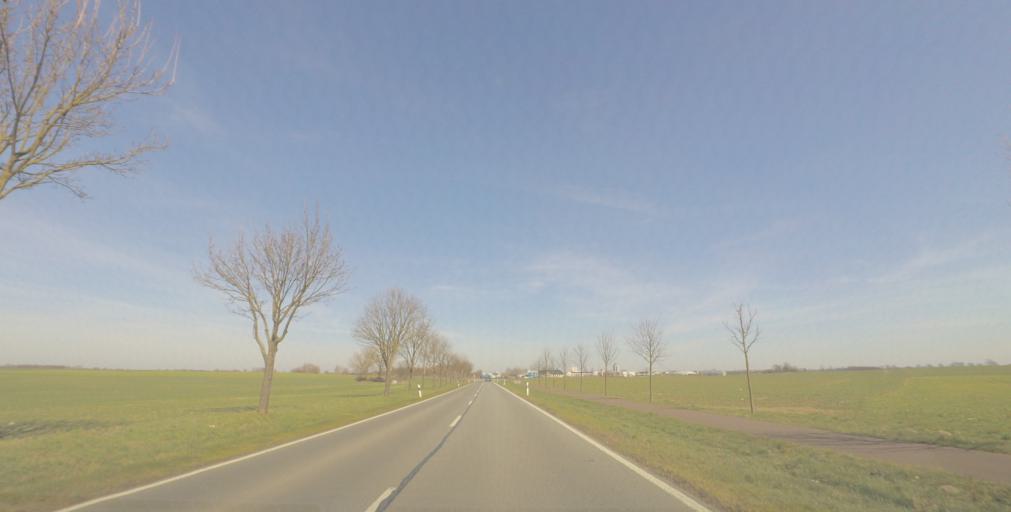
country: DE
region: Brandenburg
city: Neuruppin
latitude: 52.8726
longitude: 12.7847
